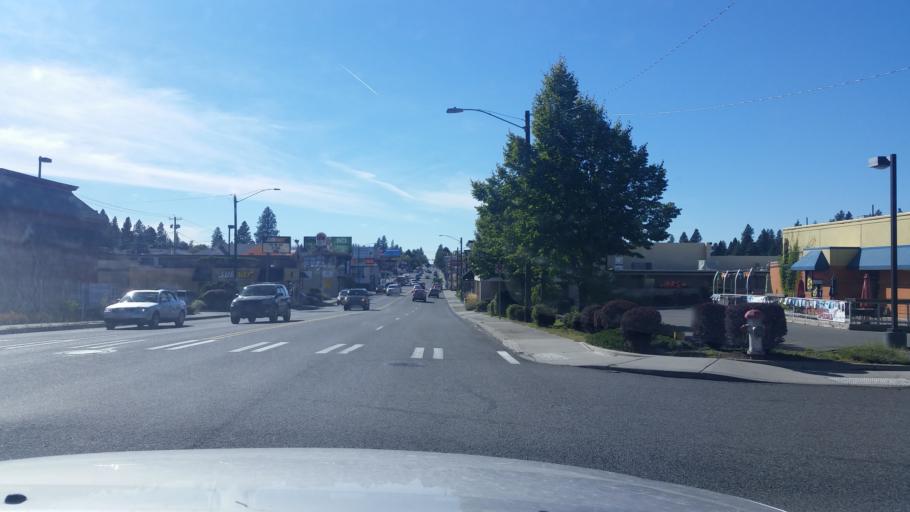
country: US
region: Washington
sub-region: Spokane County
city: Spokane
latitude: 47.6282
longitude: -117.3656
